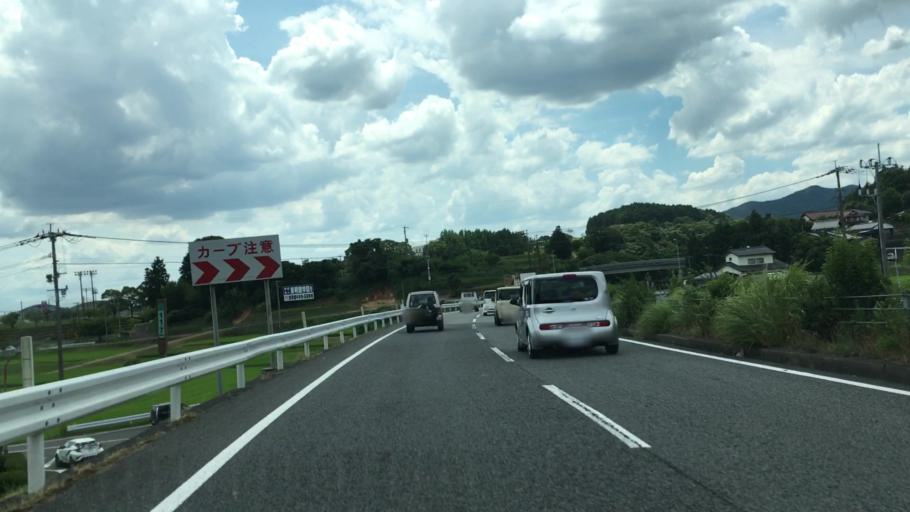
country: JP
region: Fukuoka
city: Chikushino-shi
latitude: 33.4340
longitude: 130.5243
